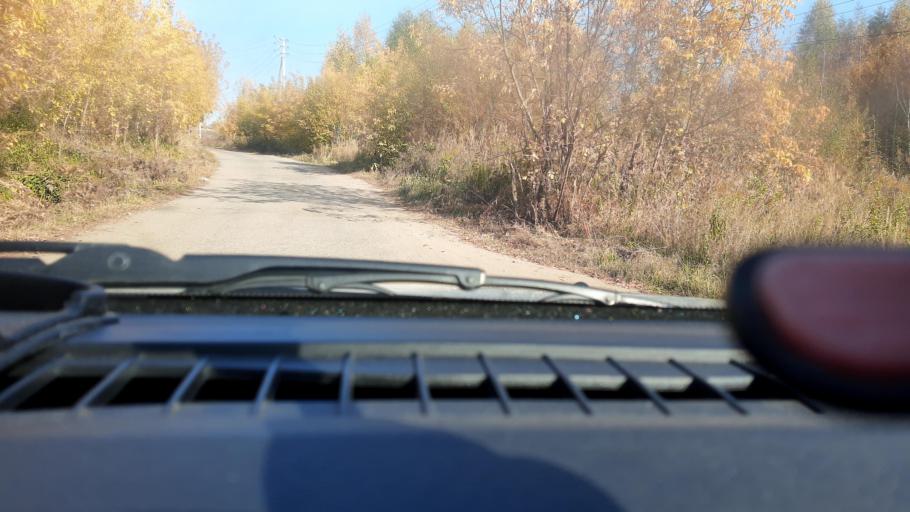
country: RU
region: Nizjnij Novgorod
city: Afonino
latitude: 56.2329
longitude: 44.0952
